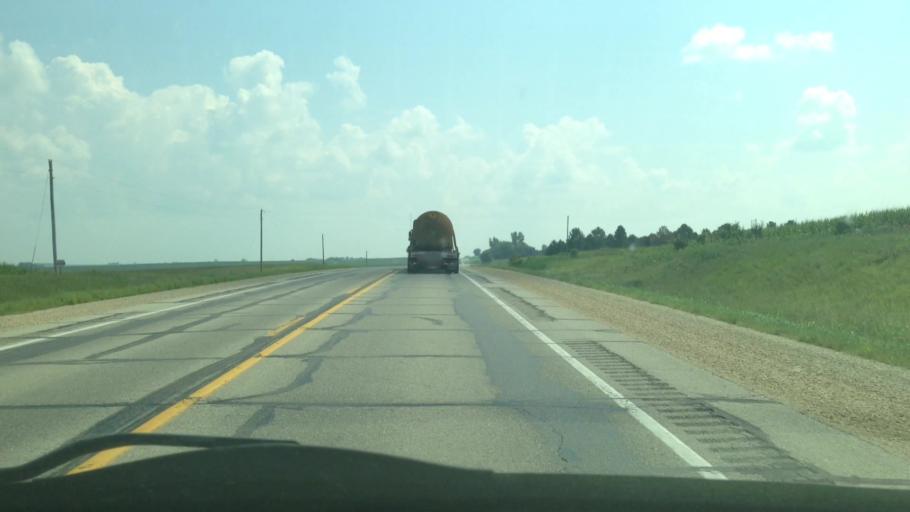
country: US
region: Iowa
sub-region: Chickasaw County
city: New Hampton
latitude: 43.1936
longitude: -92.2982
